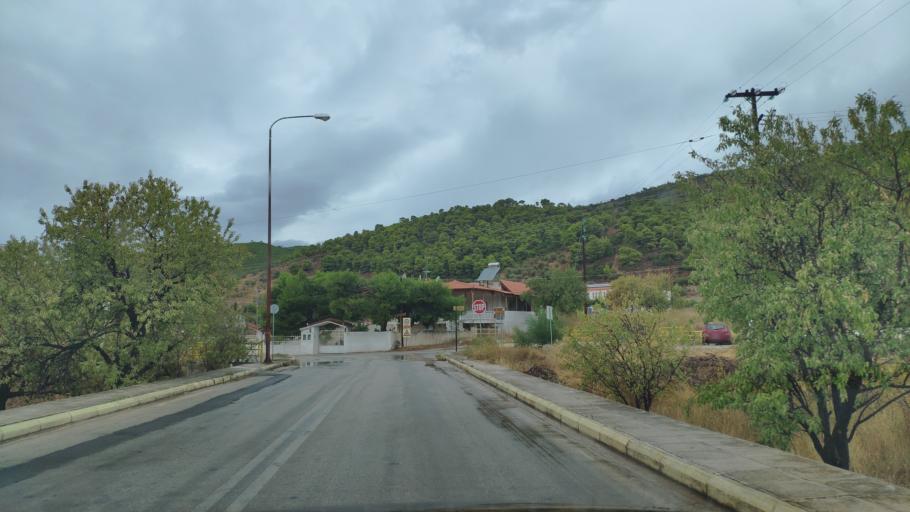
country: GR
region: Peloponnese
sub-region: Nomos Korinthias
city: Perachora
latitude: 38.0290
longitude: 22.9453
